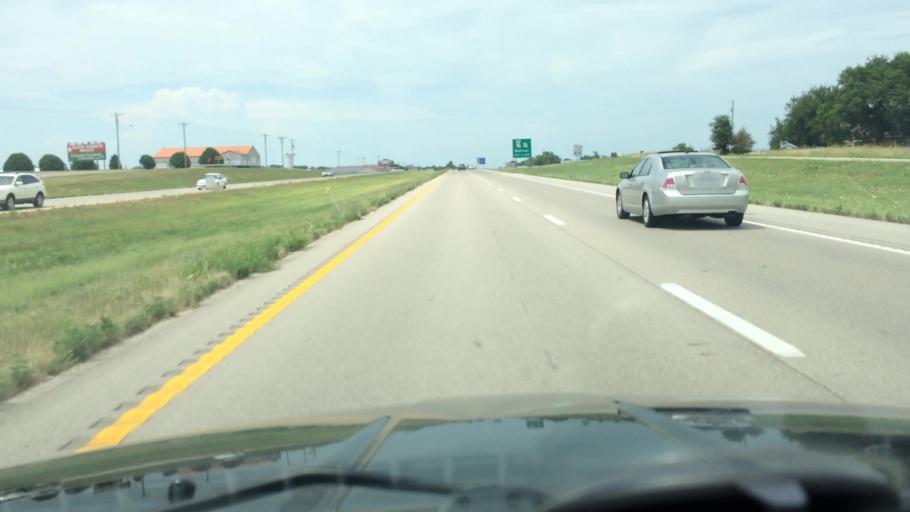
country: US
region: Missouri
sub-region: Polk County
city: Bolivar
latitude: 37.5563
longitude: -93.3890
